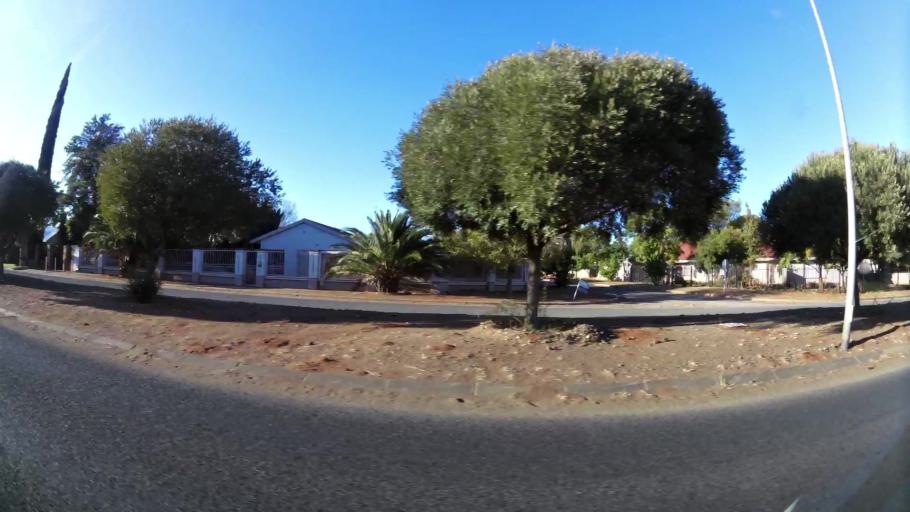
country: ZA
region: Northern Cape
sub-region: Frances Baard District Municipality
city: Kimberley
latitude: -28.7513
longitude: 24.7362
